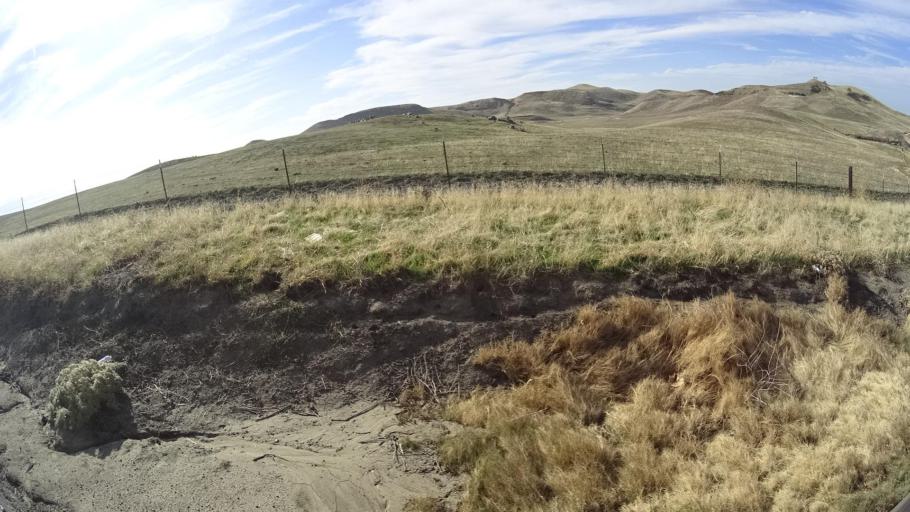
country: US
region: California
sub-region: Kern County
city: Oildale
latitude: 35.6111
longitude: -118.8661
